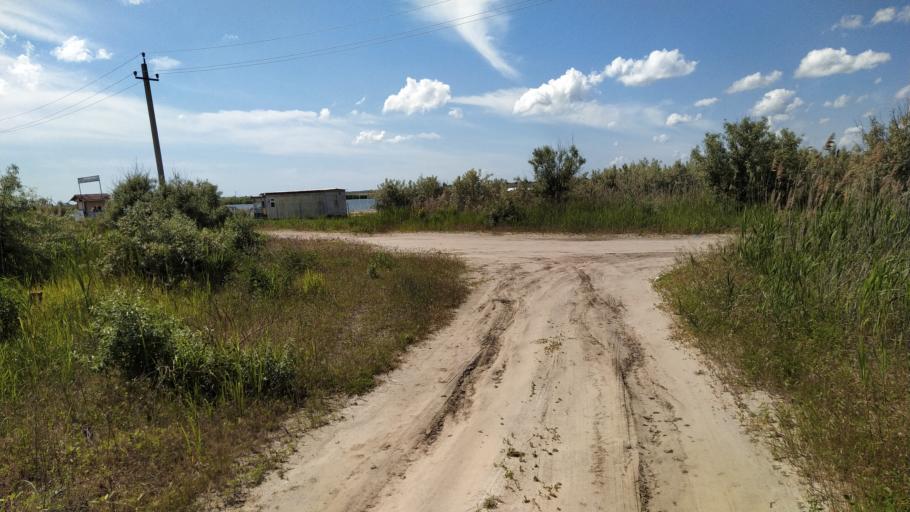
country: RU
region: Rostov
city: Bataysk
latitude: 47.1425
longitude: 39.6675
